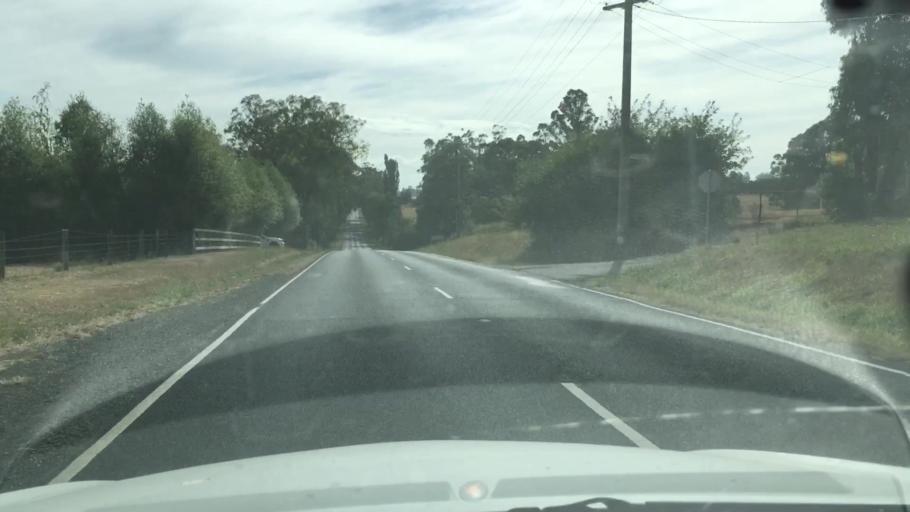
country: AU
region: Victoria
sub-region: Yarra Ranges
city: Woori Yallock
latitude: -37.8084
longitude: 145.5126
